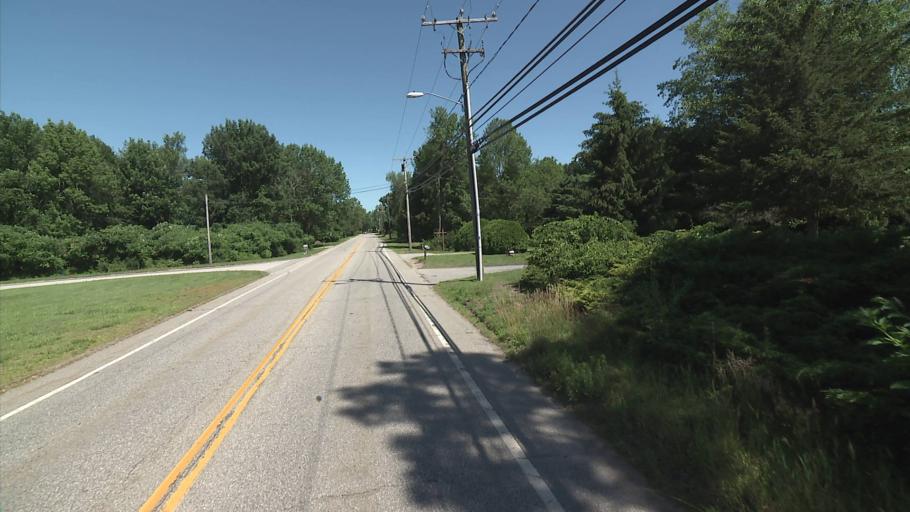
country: US
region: Connecticut
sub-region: Windham County
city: Willimantic
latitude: 41.6797
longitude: -72.2359
